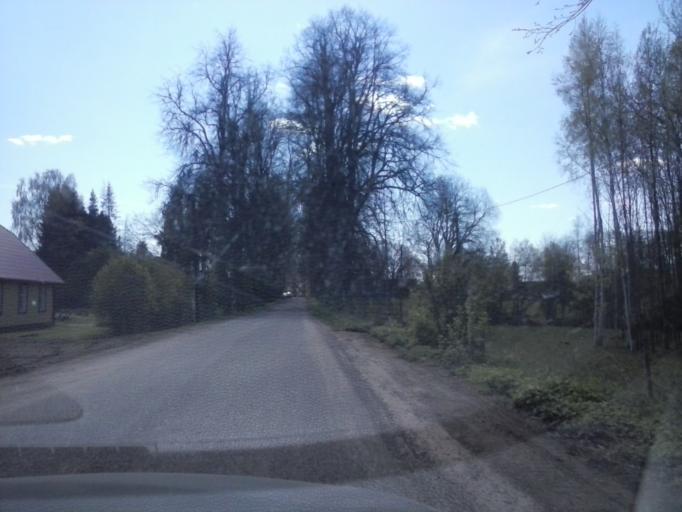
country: EE
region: Valgamaa
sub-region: Torva linn
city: Torva
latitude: 58.2301
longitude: 25.8901
